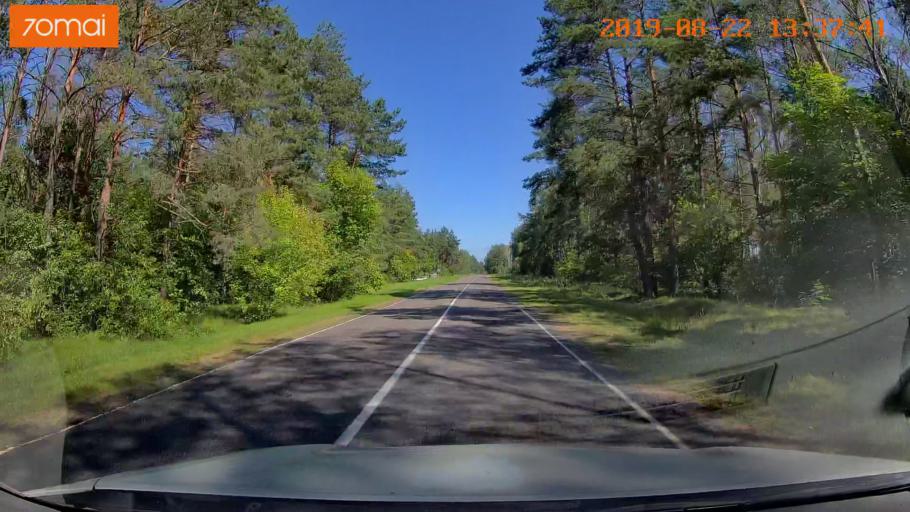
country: BY
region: Minsk
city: Staryya Darohi
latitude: 53.2170
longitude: 28.3041
